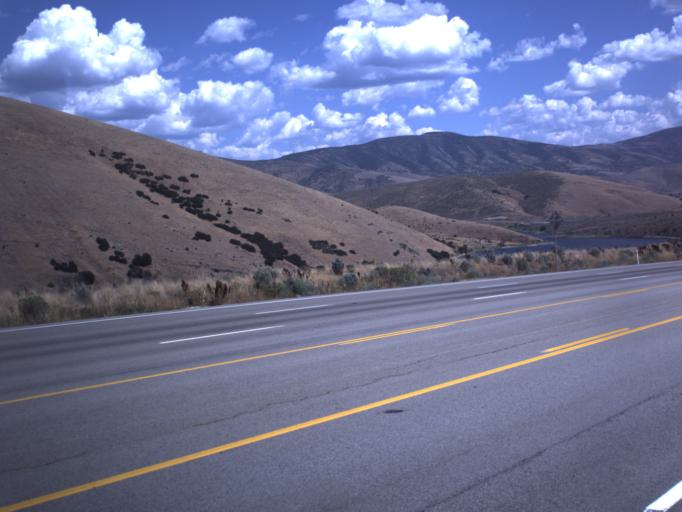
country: US
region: Utah
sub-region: Wasatch County
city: Midway
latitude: 40.4095
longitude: -111.5039
